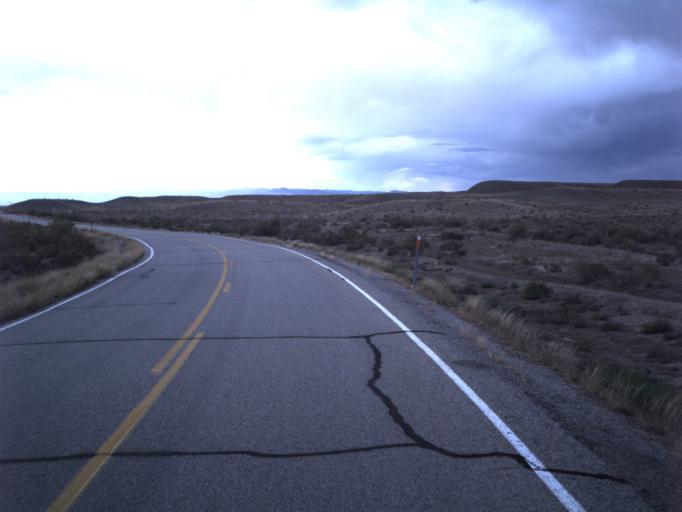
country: US
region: Utah
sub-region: Grand County
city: Moab
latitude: 38.8677
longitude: -109.2957
